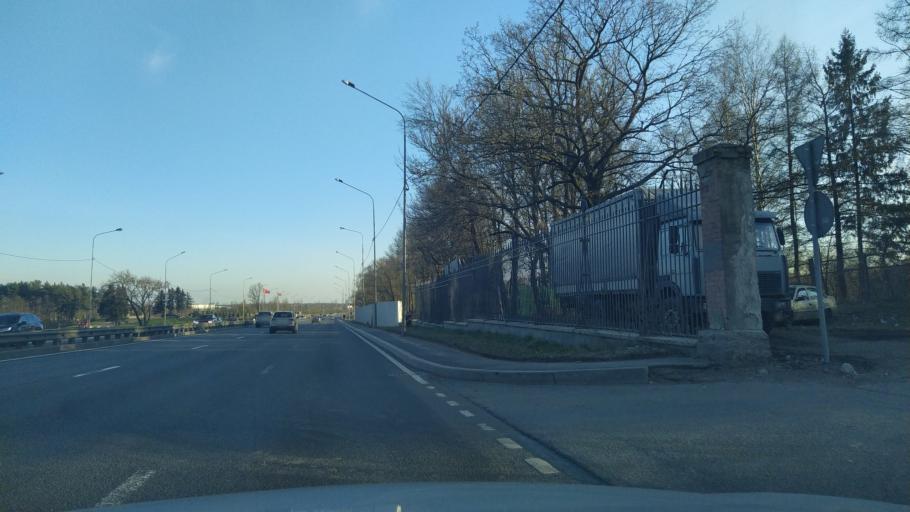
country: RU
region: St.-Petersburg
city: Aleksandrovskaya
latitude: 59.7672
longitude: 30.3309
